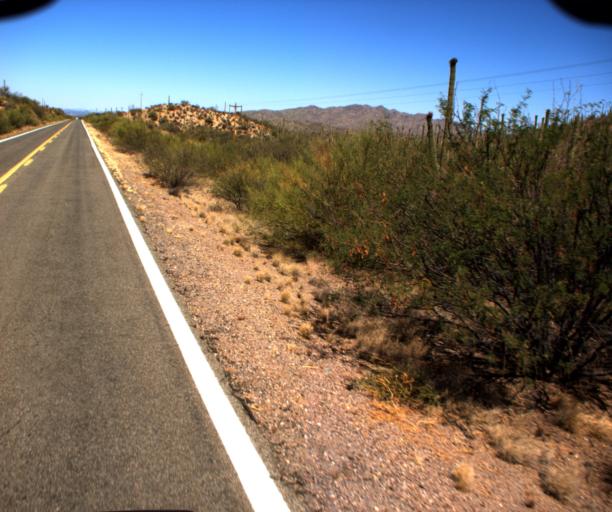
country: US
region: Arizona
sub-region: Pima County
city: Sells
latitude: 32.1743
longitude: -112.1722
